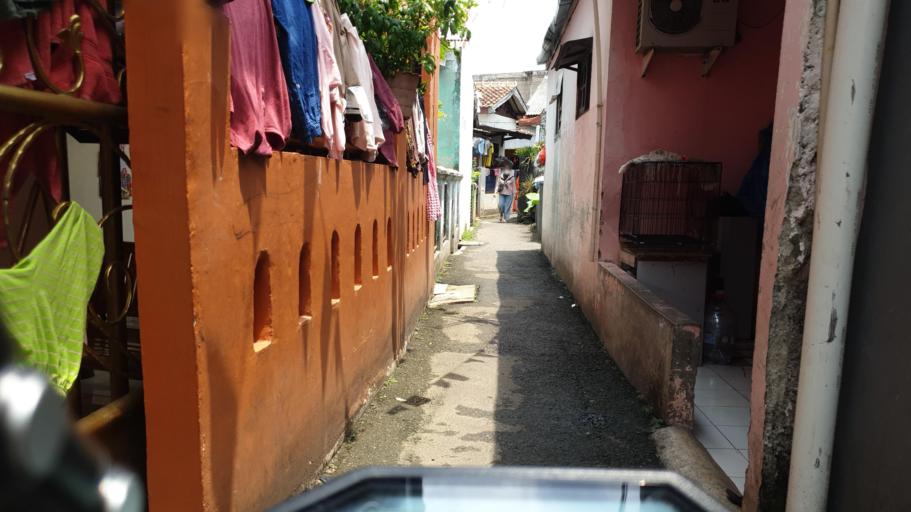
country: ID
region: West Java
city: Depok
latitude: -6.3325
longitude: 106.8301
